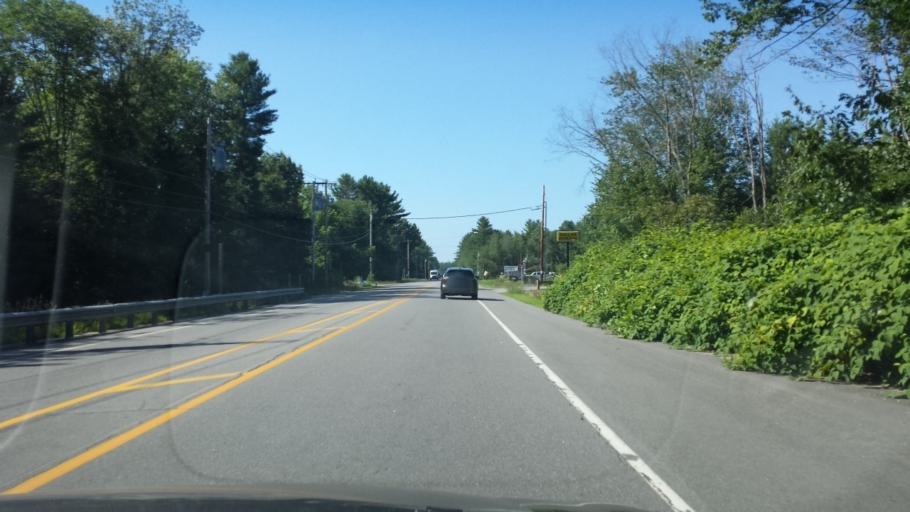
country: US
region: Maine
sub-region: York County
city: Lebanon
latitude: 43.4111
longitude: -70.8694
